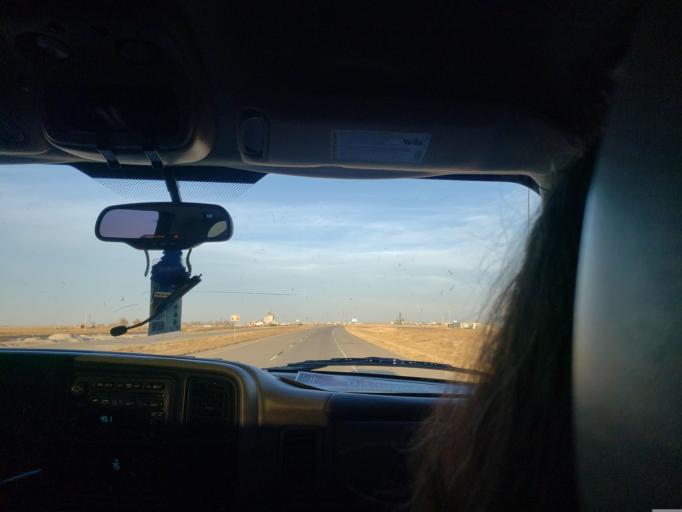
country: US
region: Oklahoma
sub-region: Texas County
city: Guymon
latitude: 36.7602
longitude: -101.3566
